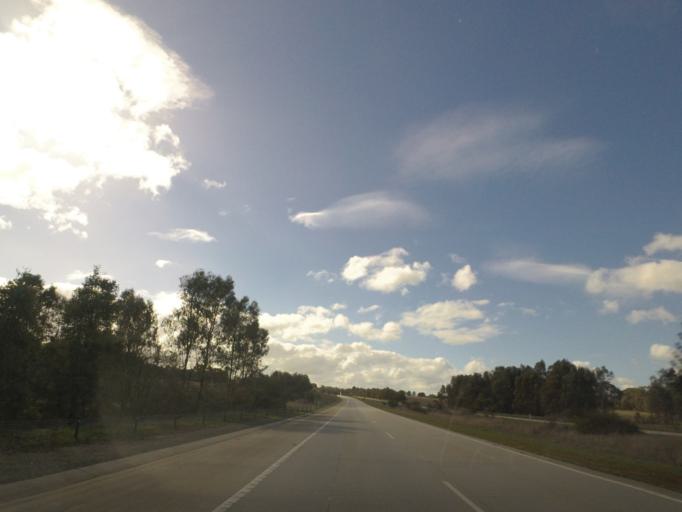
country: AU
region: New South Wales
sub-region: Albury Municipality
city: Lavington
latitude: -36.0061
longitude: 146.9900
